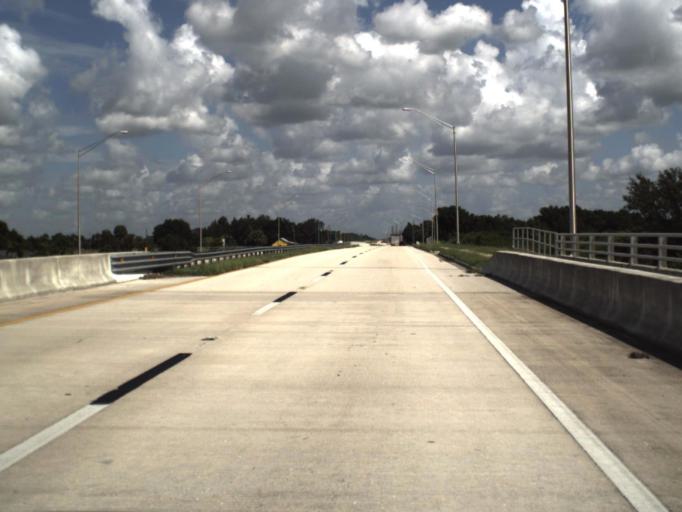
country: US
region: Florida
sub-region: Charlotte County
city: Cleveland
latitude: 26.9811
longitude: -81.9591
